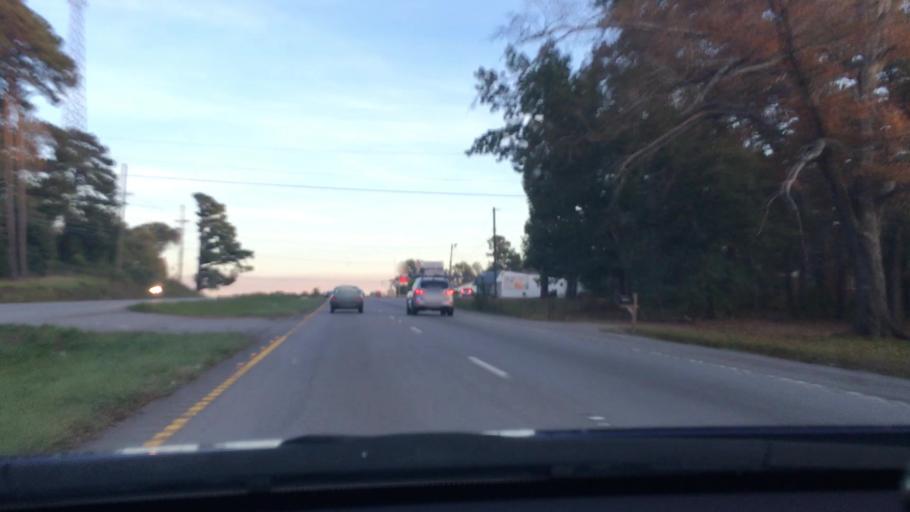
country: US
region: South Carolina
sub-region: Richland County
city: Hopkins
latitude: 33.9510
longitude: -80.8231
